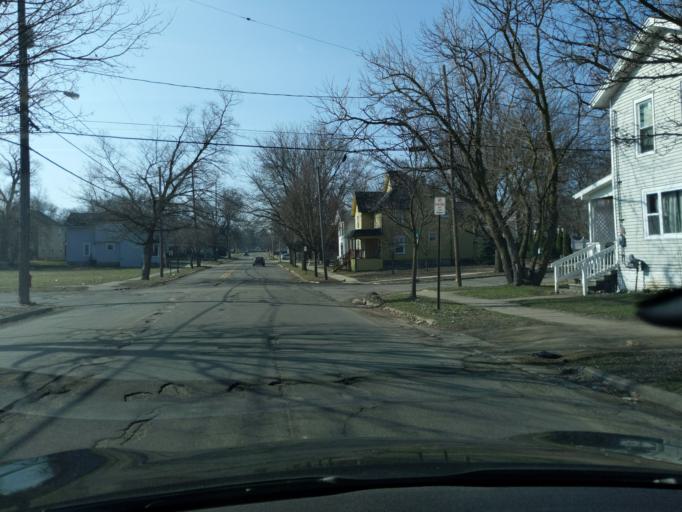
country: US
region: Michigan
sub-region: Jackson County
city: Jackson
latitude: 42.2433
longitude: -84.4118
